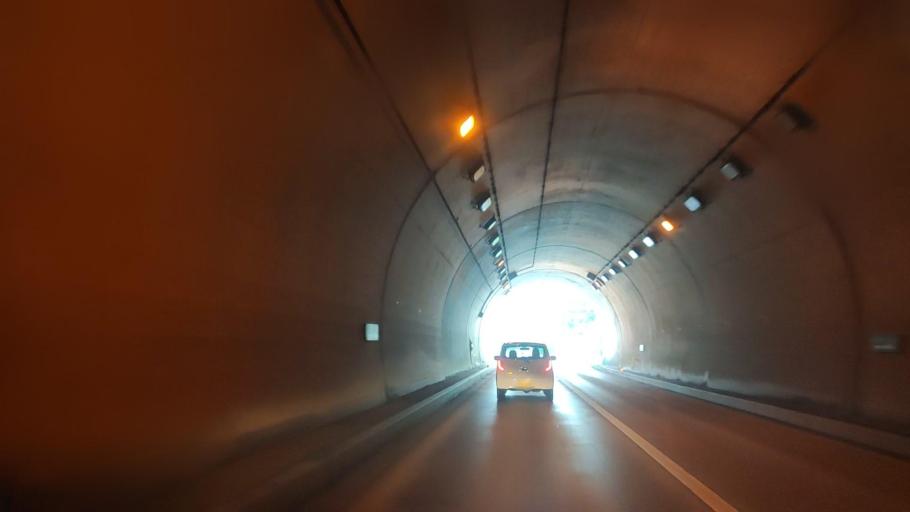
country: JP
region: Tottori
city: Kurayoshi
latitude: 35.3006
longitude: 133.7382
